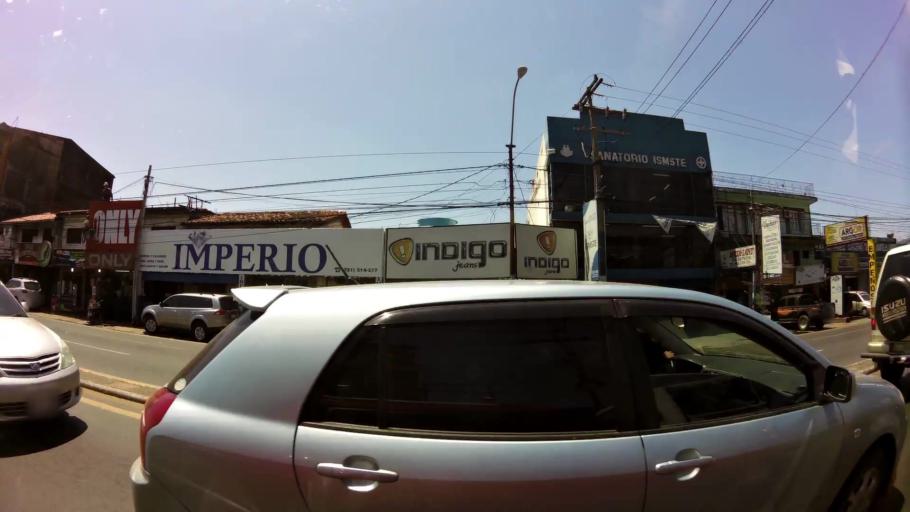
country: PY
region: Central
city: Fernando de la Mora
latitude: -25.3241
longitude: -57.5531
